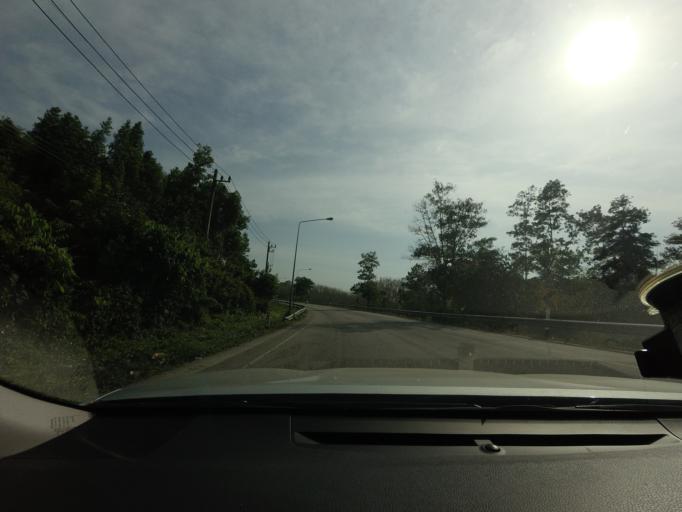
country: TH
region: Narathiwat
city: Narathiwat
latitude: 6.3687
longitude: 101.7904
